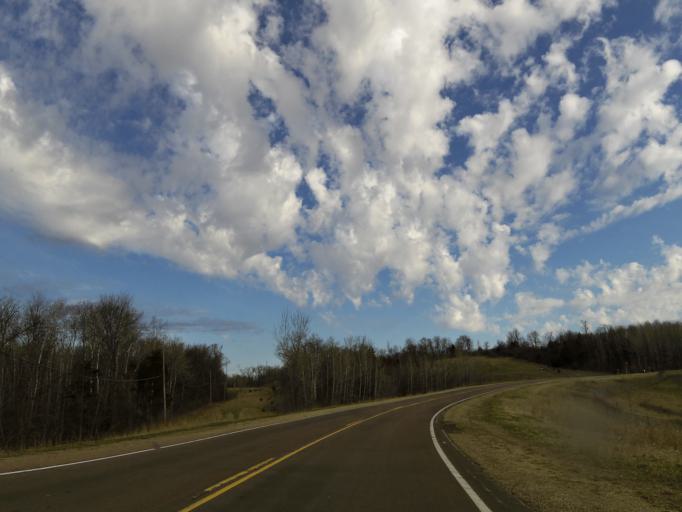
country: US
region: Minnesota
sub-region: Dakota County
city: Hastings
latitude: 44.7588
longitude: -92.8451
